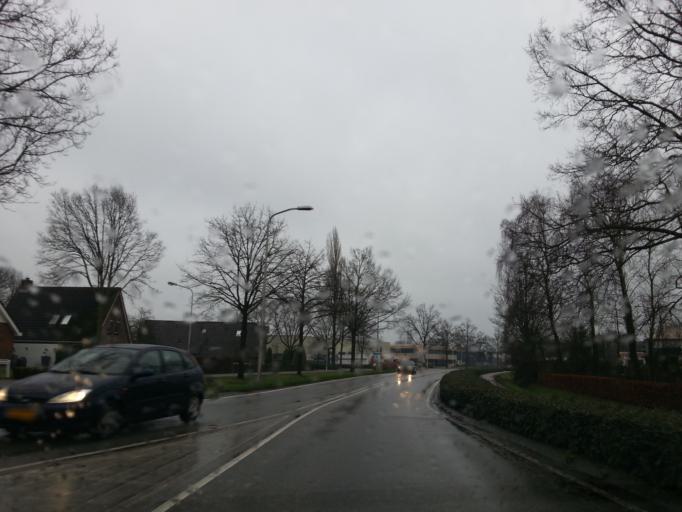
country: NL
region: Overijssel
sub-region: Gemeente Dalfsen
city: Dalfsen
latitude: 52.5129
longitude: 6.2619
